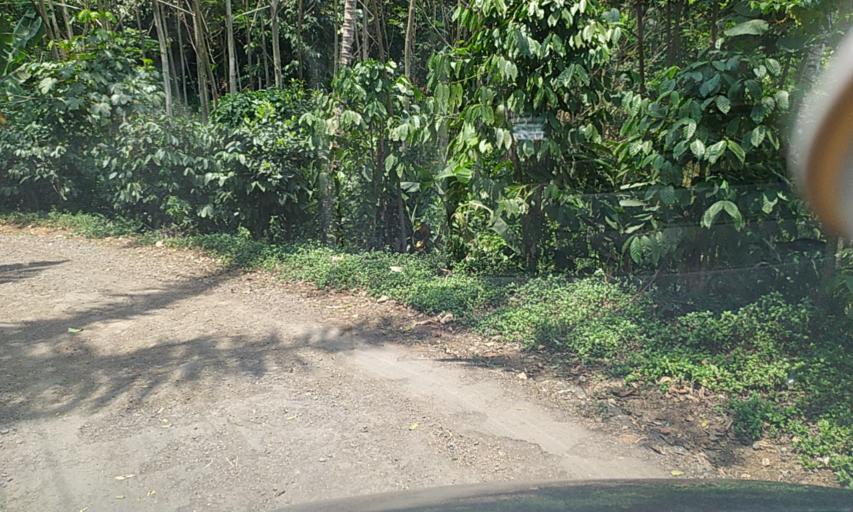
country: ID
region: Central Java
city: Kaduluhur
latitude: -7.1885
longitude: 108.6443
